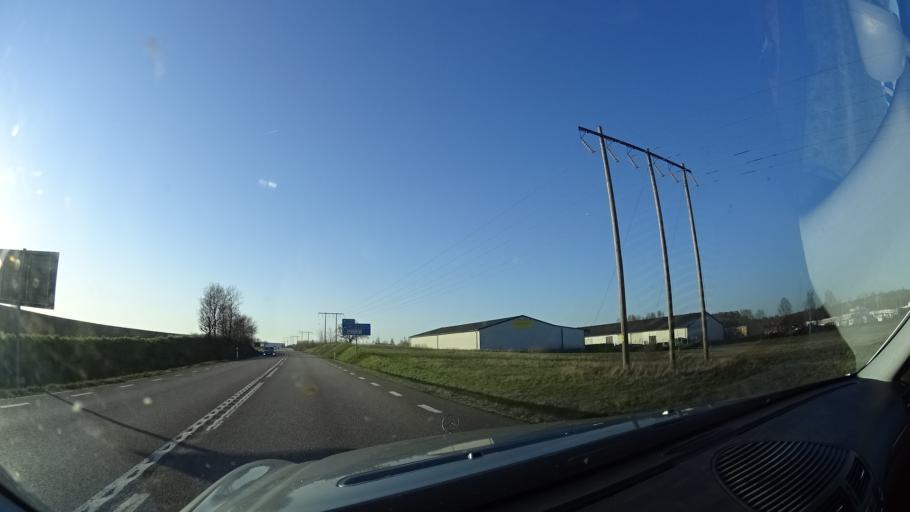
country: SE
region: Skane
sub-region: Bjuvs Kommun
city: Billesholm
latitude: 56.0532
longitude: 12.9620
